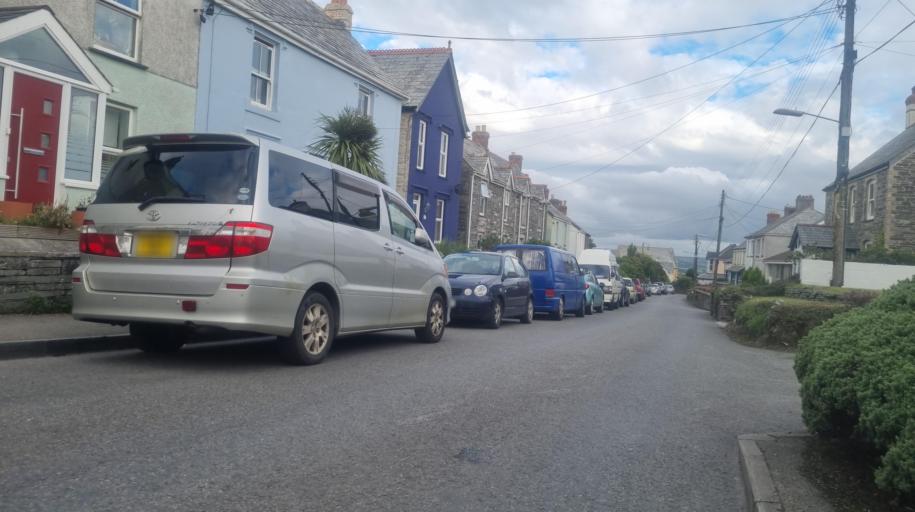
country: GB
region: England
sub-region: Cornwall
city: Tintagel
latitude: 50.6228
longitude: -4.7313
